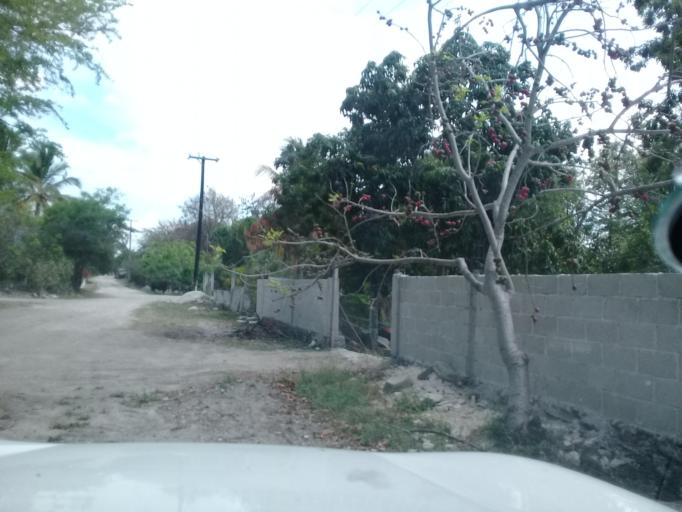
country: MX
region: Veracruz
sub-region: Emiliano Zapata
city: Plan del Rio
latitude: 19.3511
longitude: -96.6443
